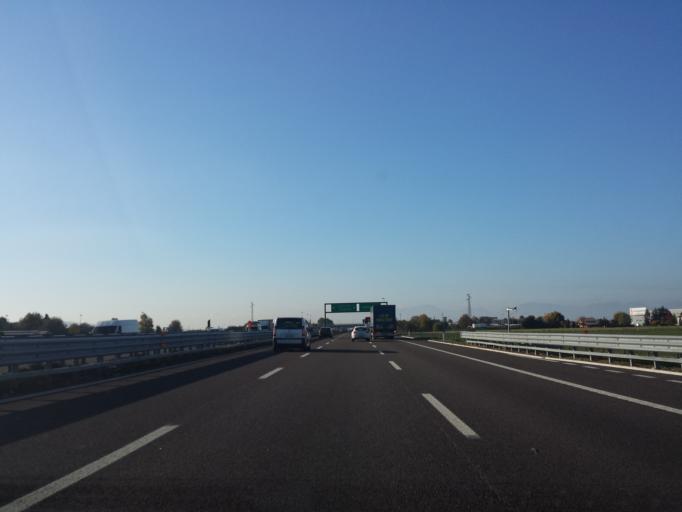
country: IT
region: Veneto
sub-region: Provincia di Vicenza
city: Grisignano di Zocco
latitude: 45.4761
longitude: 11.7139
